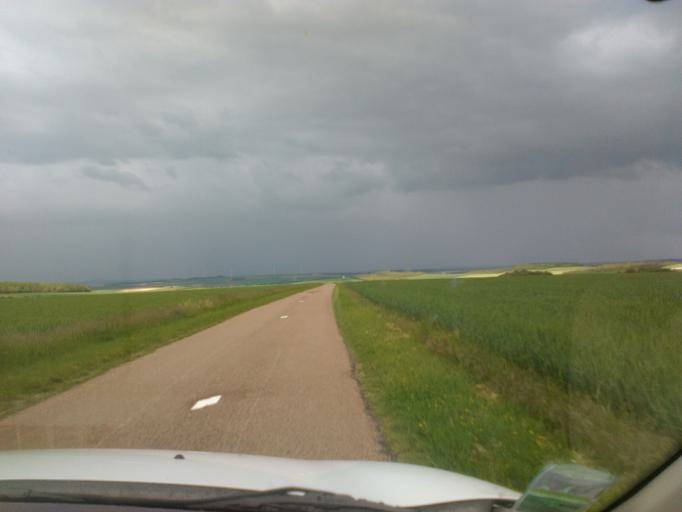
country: FR
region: Champagne-Ardenne
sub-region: Departement de l'Aube
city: Nogent-sur-Seine
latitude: 48.3767
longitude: 3.4798
